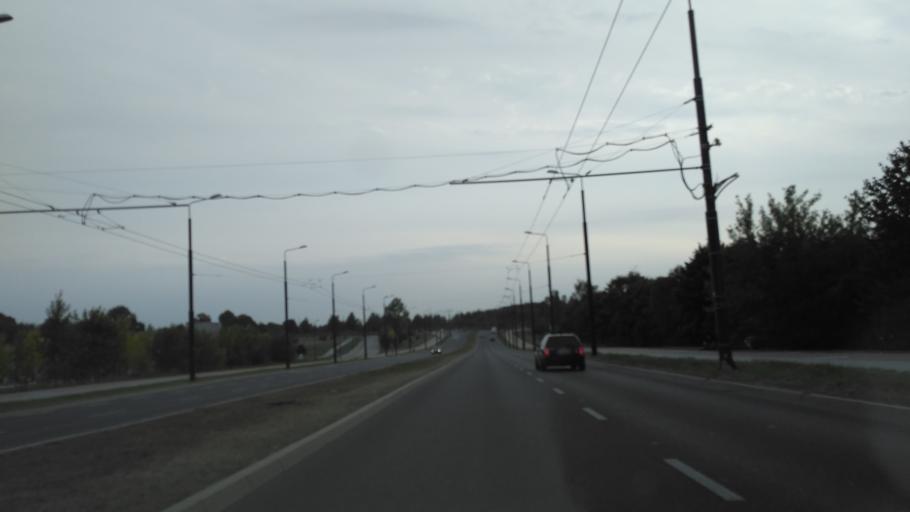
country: PL
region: Lublin Voivodeship
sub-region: Powiat lubelski
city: Jakubowice Murowane
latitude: 51.2270
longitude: 22.6179
